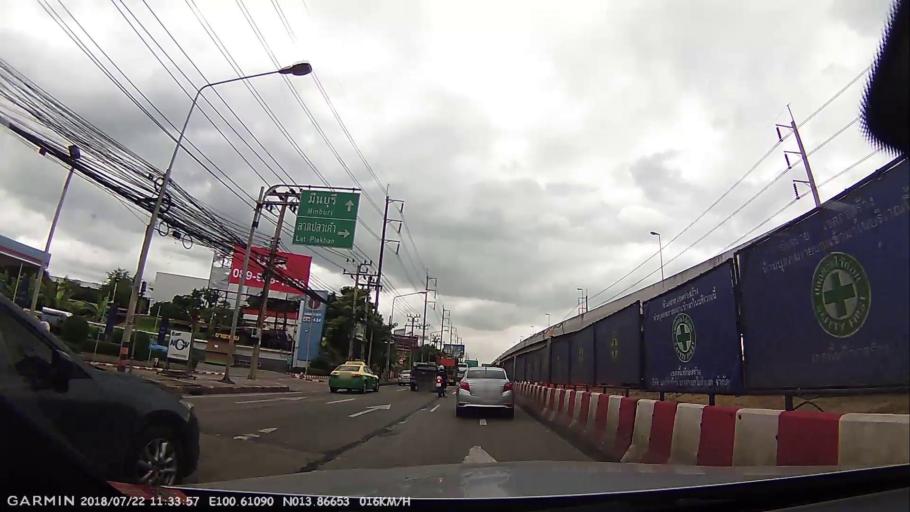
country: TH
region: Bangkok
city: Bang Khen
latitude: 13.8665
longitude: 100.6109
